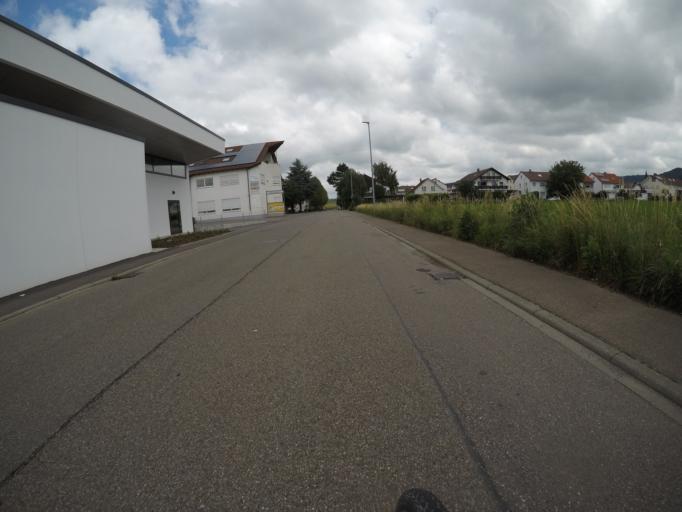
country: DE
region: Baden-Wuerttemberg
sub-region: Regierungsbezirk Stuttgart
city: Salach
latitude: 48.6936
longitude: 9.7319
